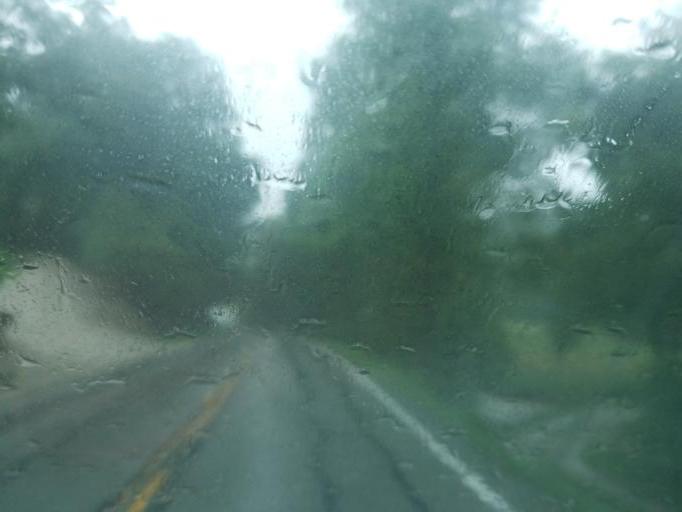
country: US
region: Kentucky
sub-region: Carter County
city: Olive Hill
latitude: 38.2840
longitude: -83.3002
